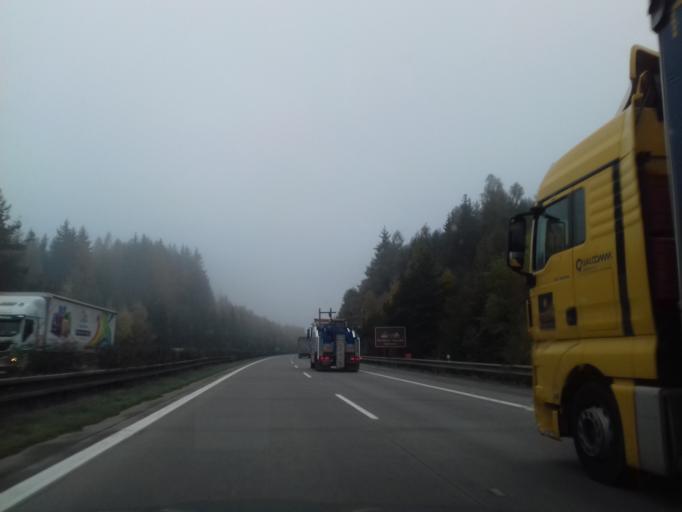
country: CZ
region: Vysocina
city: Vilemov
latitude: 49.5153
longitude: 15.4082
